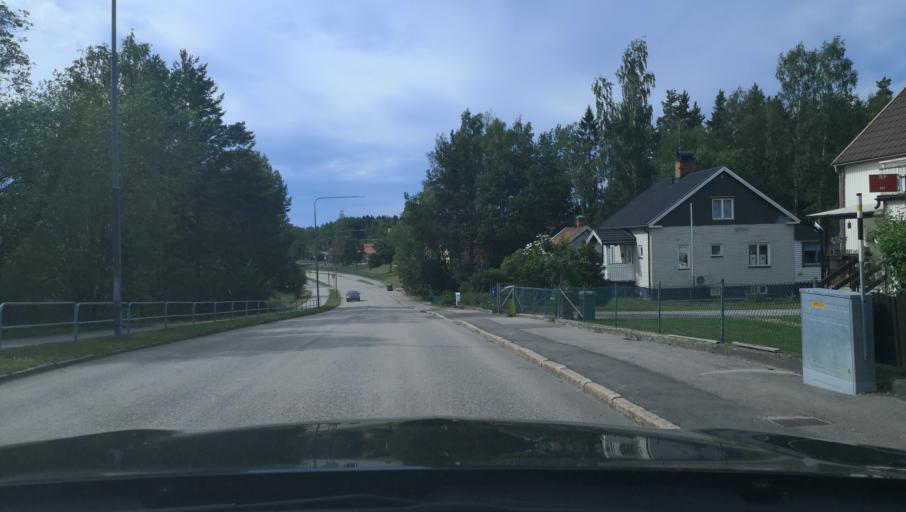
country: SE
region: Vaestmanland
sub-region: Fagersta Kommun
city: Fagersta
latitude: 59.9895
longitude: 15.8304
